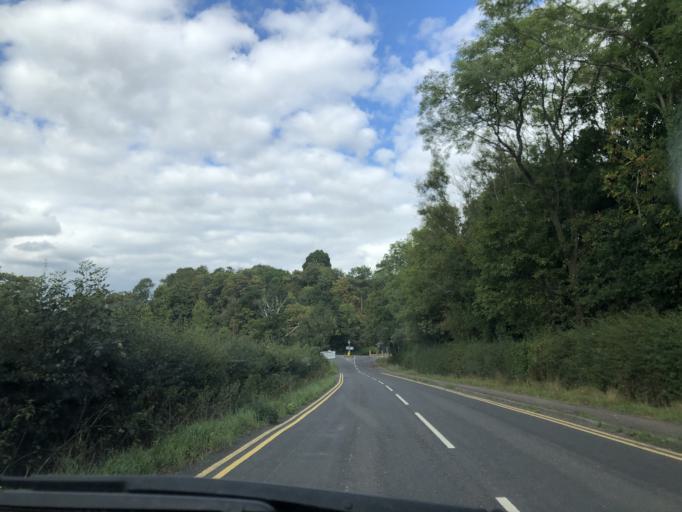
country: GB
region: England
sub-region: Kent
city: Tonbridge
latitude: 51.2205
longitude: 0.2293
